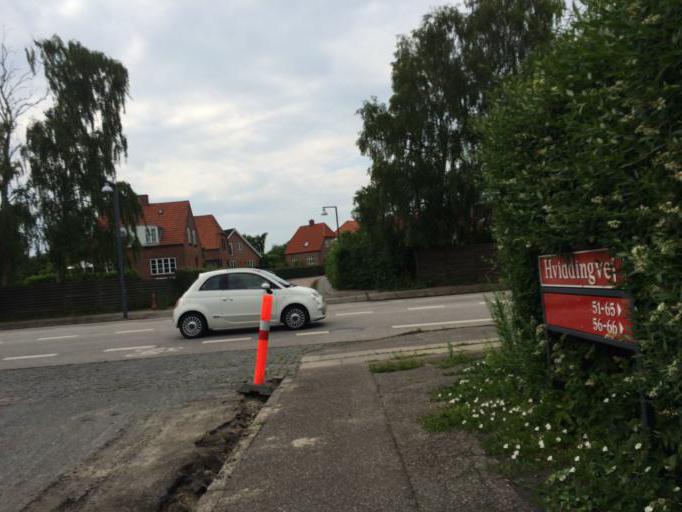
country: DK
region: Capital Region
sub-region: Hvidovre Kommune
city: Hvidovre
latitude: 55.6669
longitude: 12.4627
